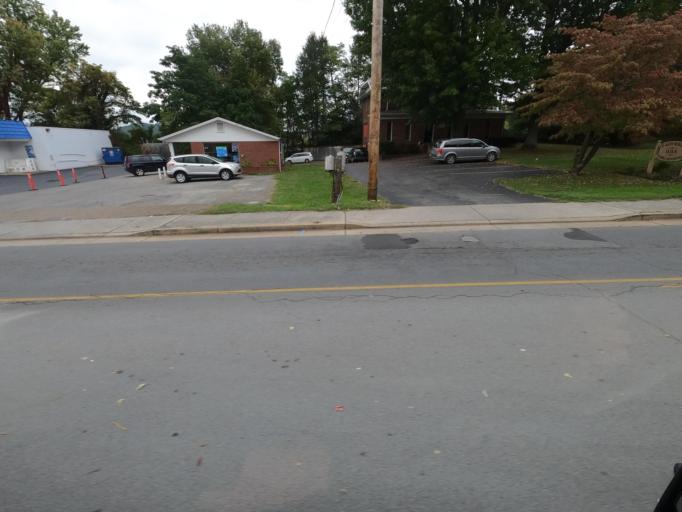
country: US
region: Tennessee
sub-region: Carter County
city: Elizabethton
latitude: 36.3445
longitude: -82.2360
